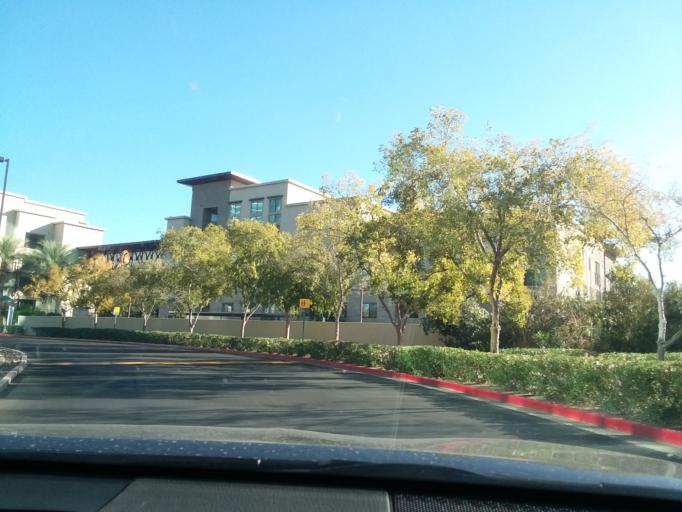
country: US
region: Arizona
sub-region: Maricopa County
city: Phoenix
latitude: 33.5079
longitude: -112.0257
